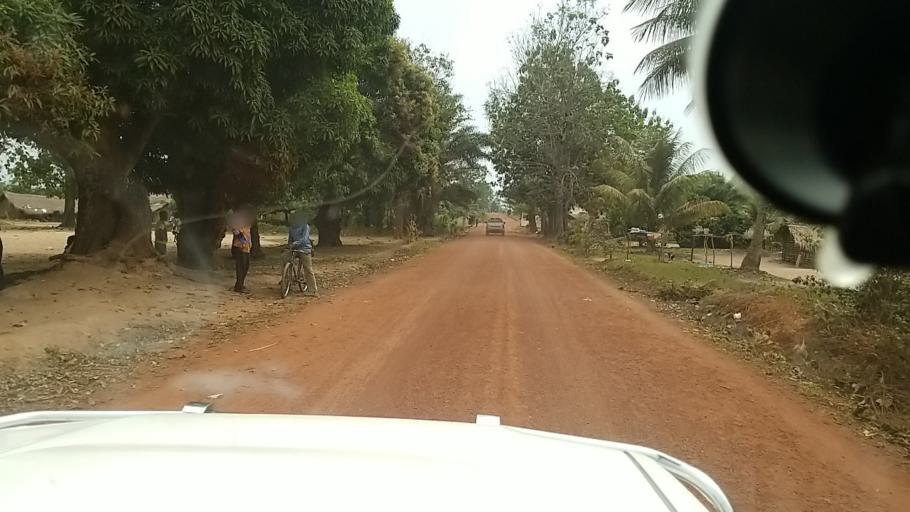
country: CD
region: Equateur
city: Libenge
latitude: 3.7190
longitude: 18.7702
